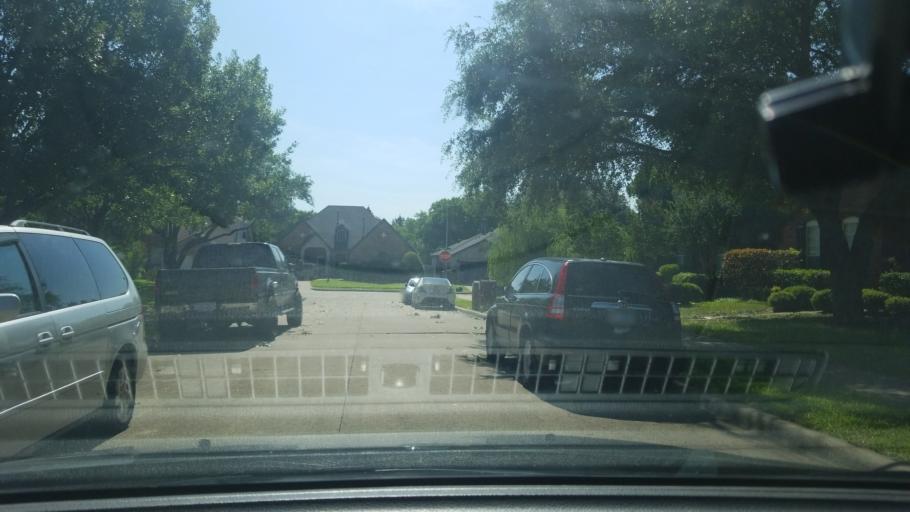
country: US
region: Texas
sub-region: Dallas County
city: Mesquite
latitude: 32.7768
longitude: -96.5833
